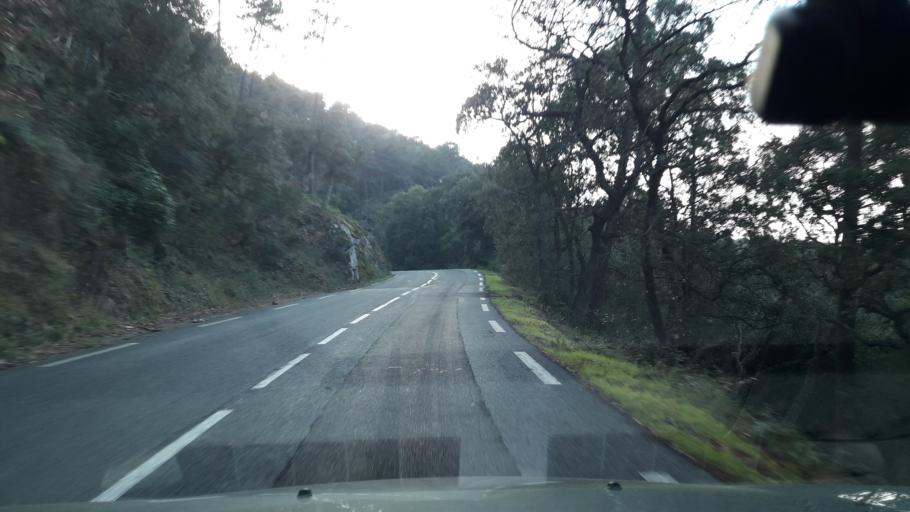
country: FR
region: Provence-Alpes-Cote d'Azur
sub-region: Departement du Var
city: Tanneron
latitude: 43.5182
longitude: 6.8522
